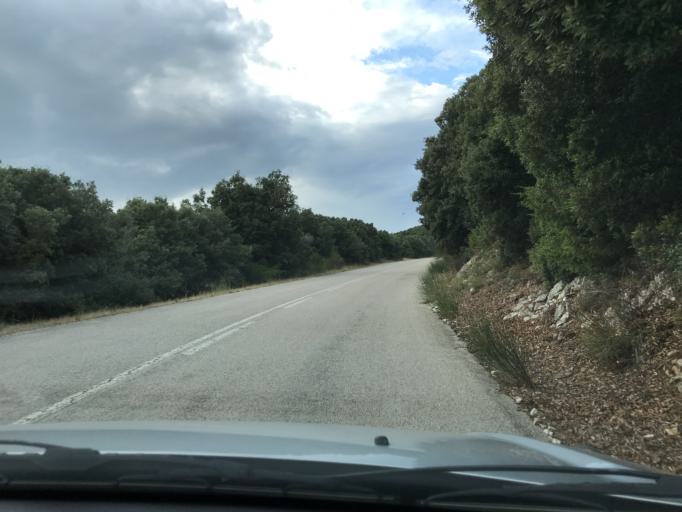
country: IT
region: Umbria
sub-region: Provincia di Terni
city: Montecchio
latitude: 42.6885
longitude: 12.2953
